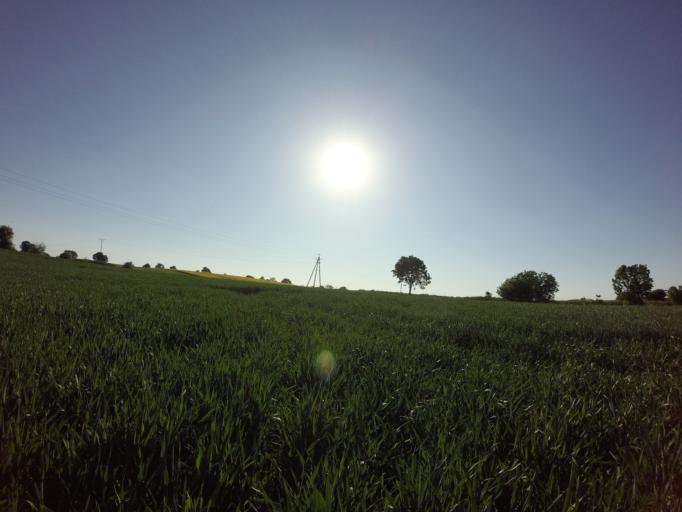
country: PL
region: West Pomeranian Voivodeship
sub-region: Powiat choszczenski
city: Choszczno
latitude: 53.1363
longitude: 15.3691
